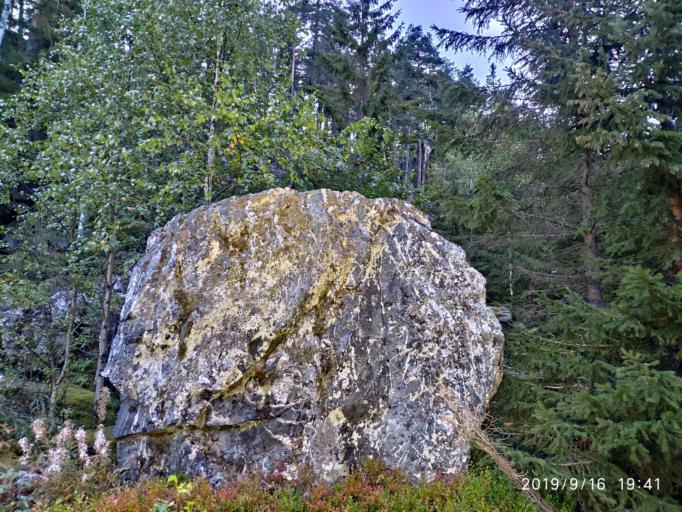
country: NO
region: Oppland
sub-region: Oyer
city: Tretten
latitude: 61.3124
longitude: 10.2825
